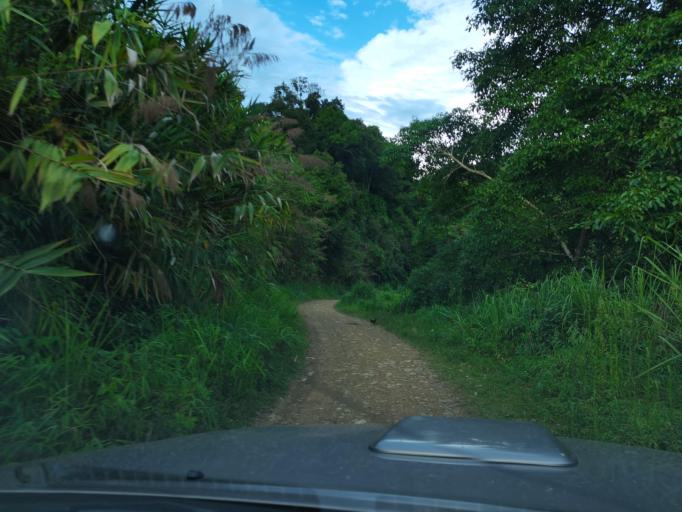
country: LA
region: Phongsali
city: Phongsali
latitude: 21.6753
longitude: 102.1888
